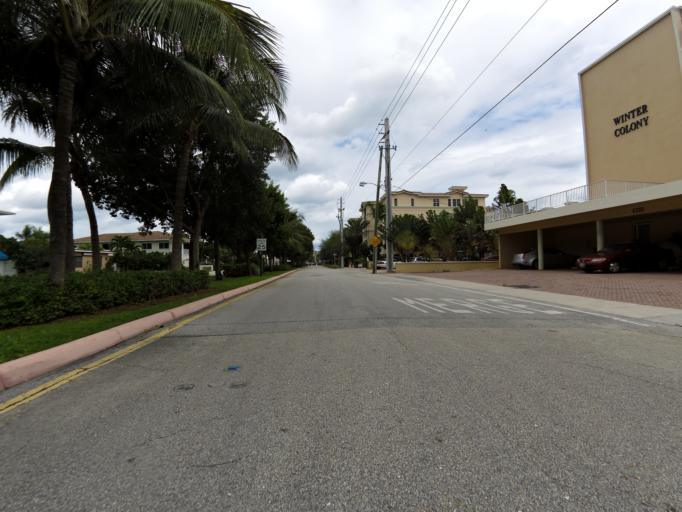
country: US
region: Florida
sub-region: Broward County
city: Lauderdale-by-the-Sea
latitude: 26.1876
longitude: -80.0959
